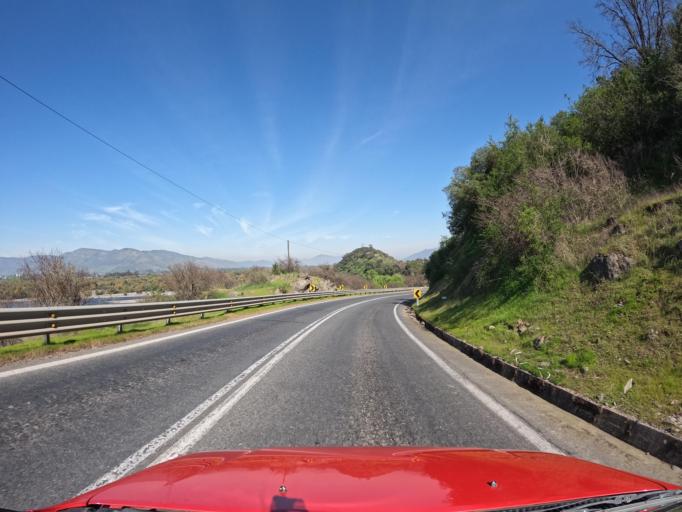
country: CL
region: Maule
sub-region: Provincia de Curico
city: Rauco
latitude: -34.9763
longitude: -71.3845
